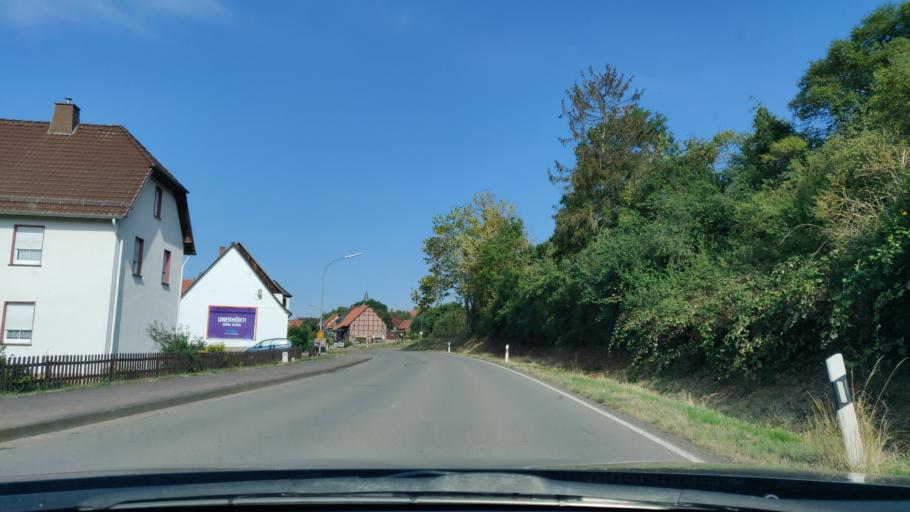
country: DE
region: Hesse
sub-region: Regierungsbezirk Kassel
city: Bad Wildungen
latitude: 51.1659
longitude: 9.1424
